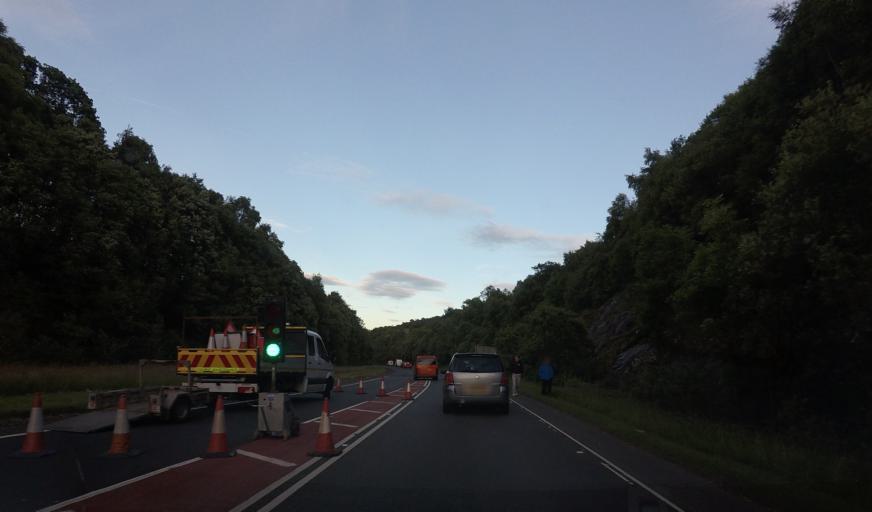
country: GB
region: Scotland
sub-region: Argyll and Bute
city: Helensburgh
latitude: 56.1689
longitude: -4.6763
